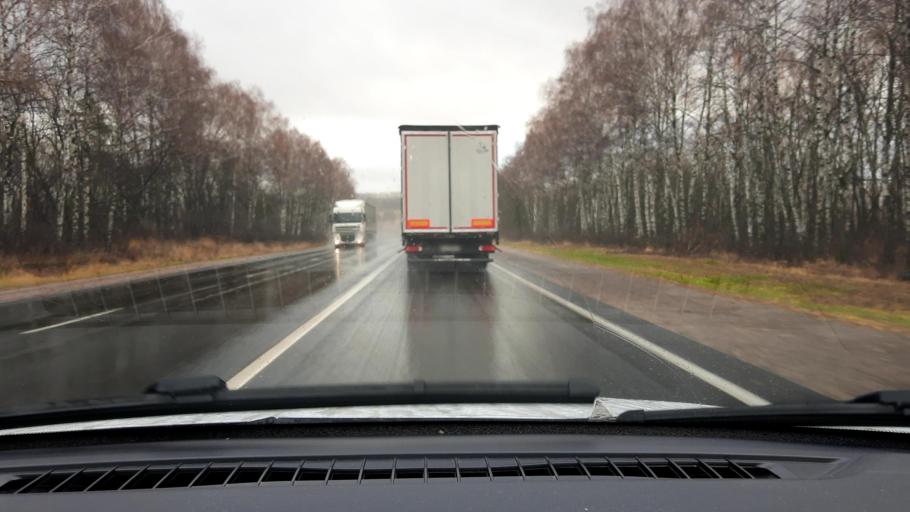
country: RU
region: Nizjnij Novgorod
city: Pamyat' Parizhskoy Kommuny
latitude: 56.0506
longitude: 44.4126
